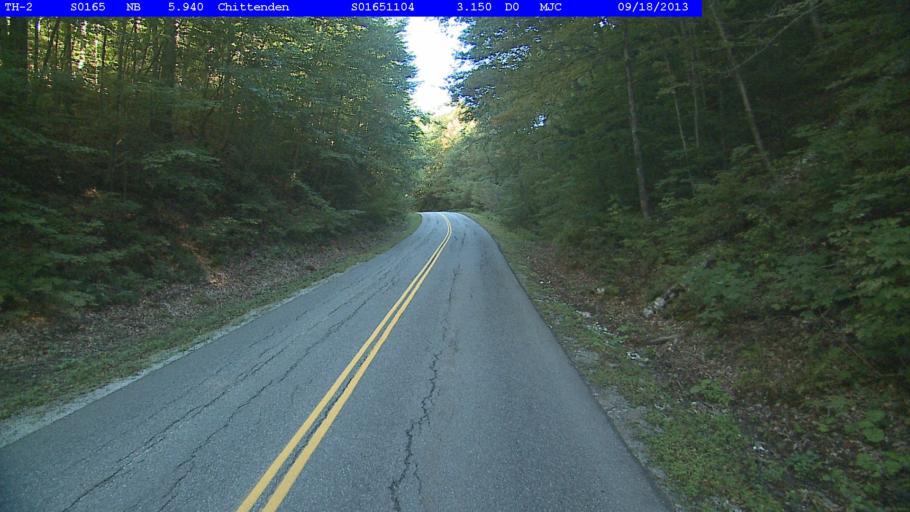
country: US
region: Vermont
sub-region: Rutland County
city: Rutland
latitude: 43.7202
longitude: -72.9655
